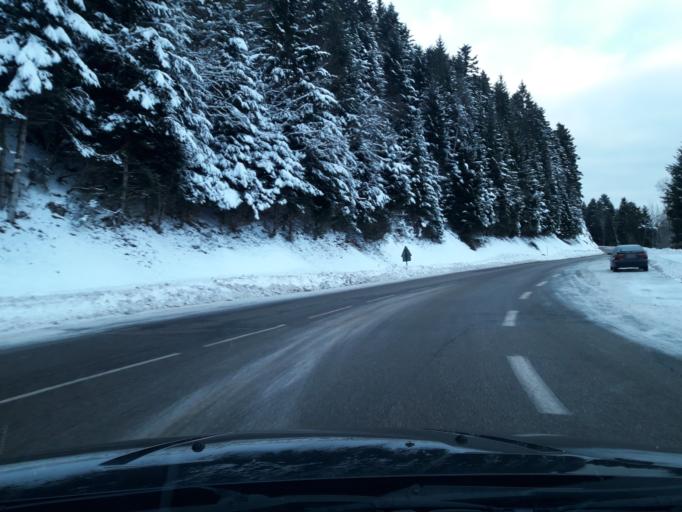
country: FR
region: Rhone-Alpes
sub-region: Departement de l'Isere
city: Revel
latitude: 45.1412
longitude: 5.8879
